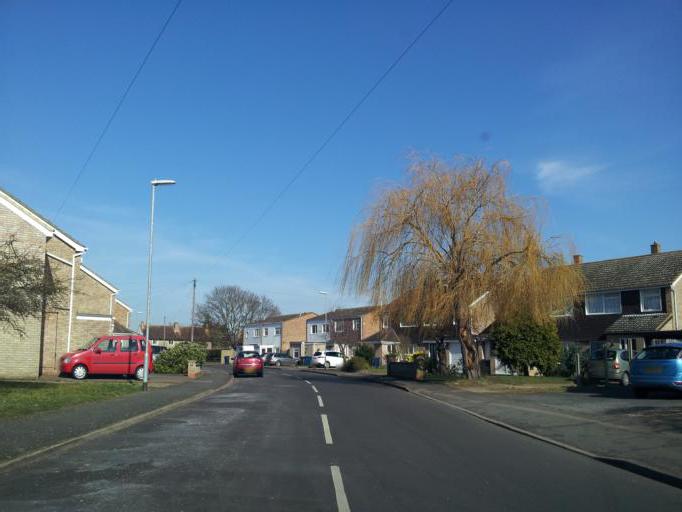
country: GB
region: England
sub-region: Cambridgeshire
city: Little Paxton
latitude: 52.2490
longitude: -0.2587
